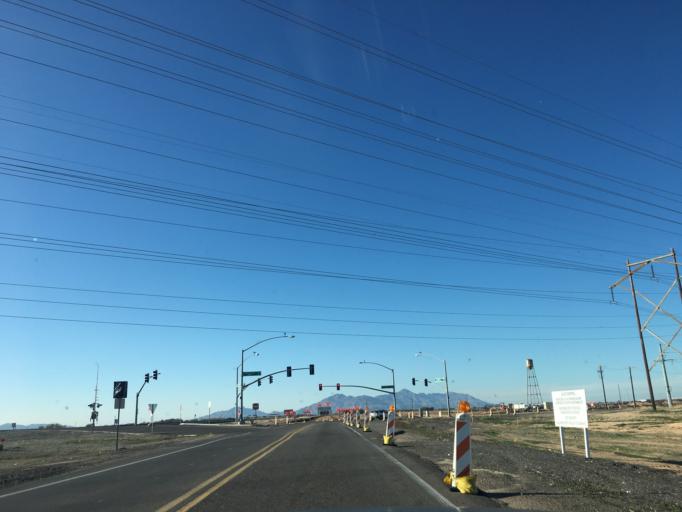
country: US
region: Arizona
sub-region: Pinal County
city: Maricopa
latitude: 33.0244
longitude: -111.9957
